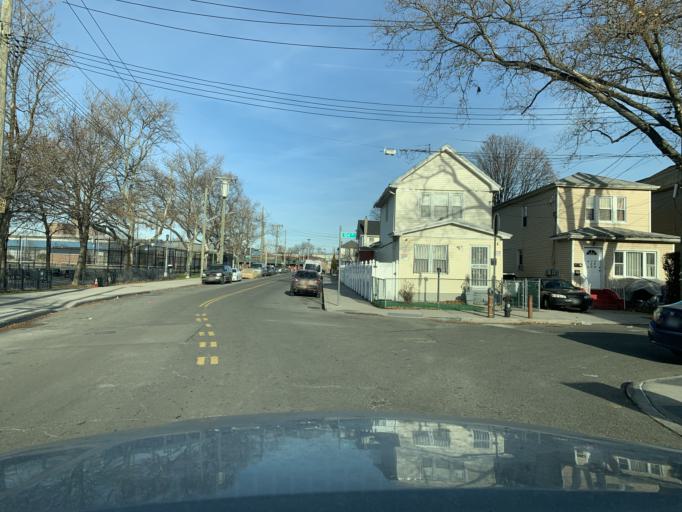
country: US
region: New York
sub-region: Queens County
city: Jamaica
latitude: 40.7032
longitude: -73.7838
